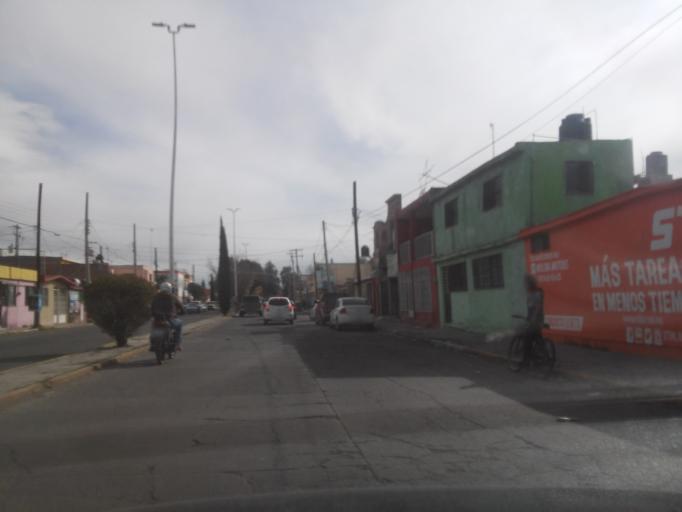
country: MX
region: Durango
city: Victoria de Durango
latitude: 24.0109
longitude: -104.6549
